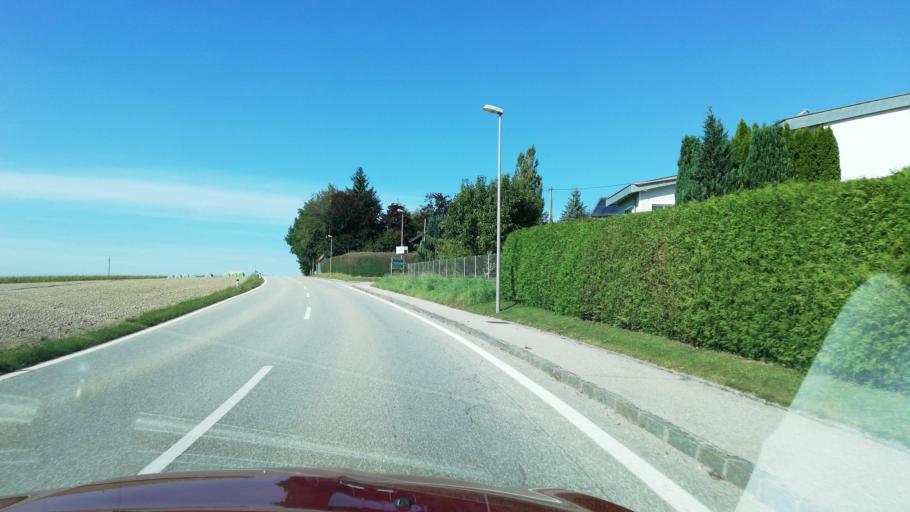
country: AT
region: Upper Austria
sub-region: Politischer Bezirk Vocklabruck
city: Zell am Pettenfirst
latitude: 48.1491
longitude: 13.5682
